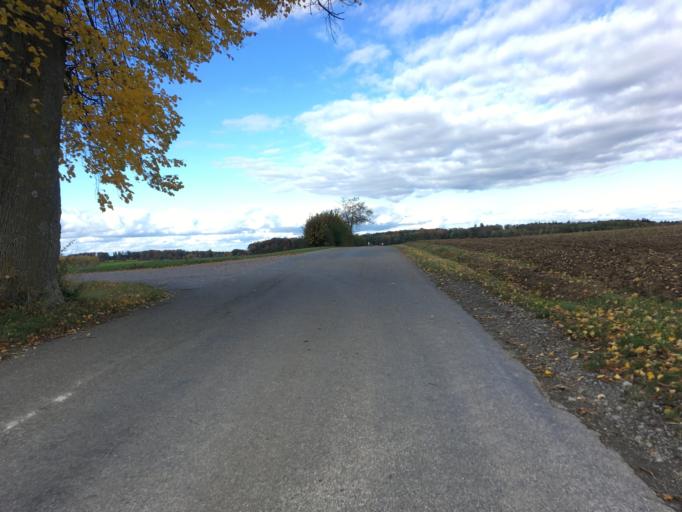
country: DE
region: Baden-Wuerttemberg
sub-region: Regierungsbezirk Stuttgart
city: Kupferzell
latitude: 49.2358
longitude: 9.7411
